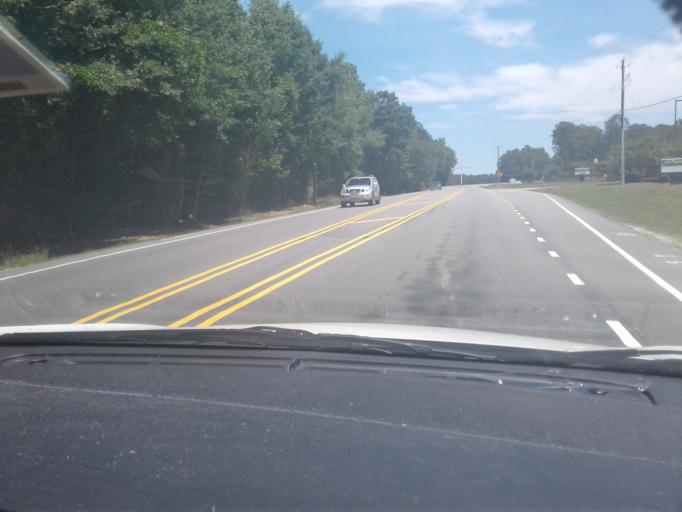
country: US
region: North Carolina
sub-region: Harnett County
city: Lillington
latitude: 35.4716
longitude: -78.8271
